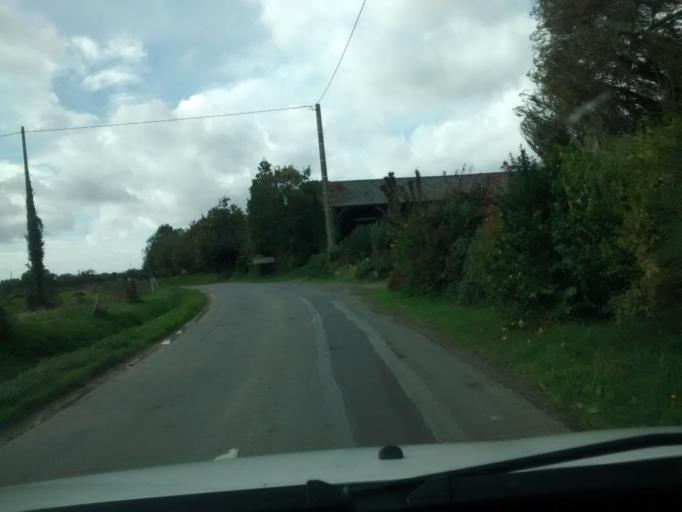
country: FR
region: Brittany
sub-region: Departement d'Ille-et-Vilaine
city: Chateaubourg
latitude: 48.1301
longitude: -1.4183
